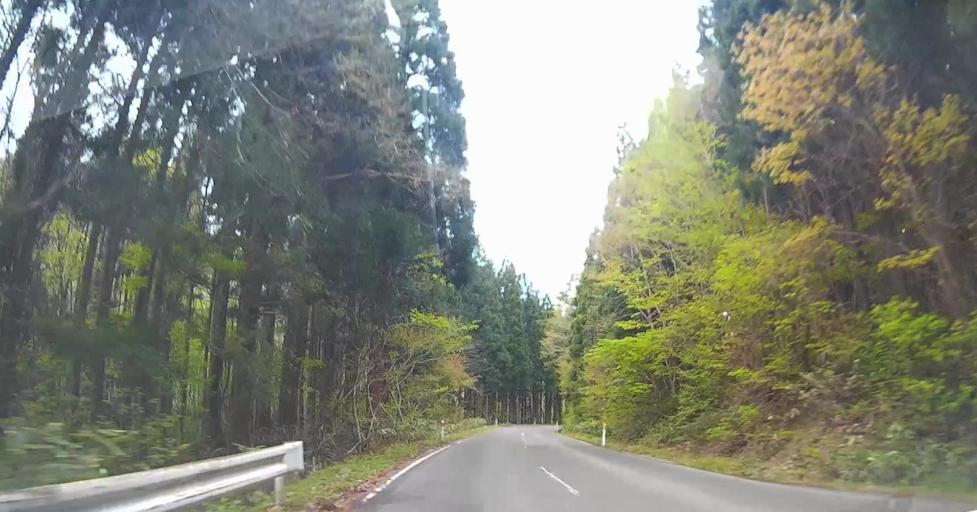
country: JP
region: Aomori
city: Goshogawara
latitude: 40.9050
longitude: 140.5115
